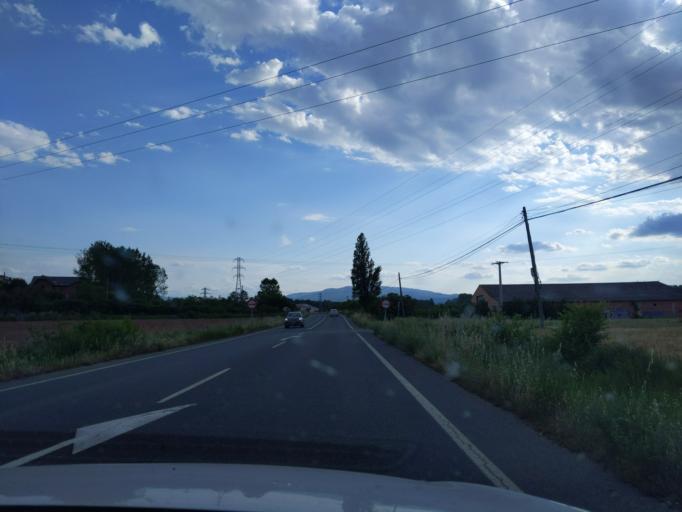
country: ES
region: La Rioja
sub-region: Provincia de La Rioja
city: Villamediana de Iregua
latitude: 42.4214
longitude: -2.4277
